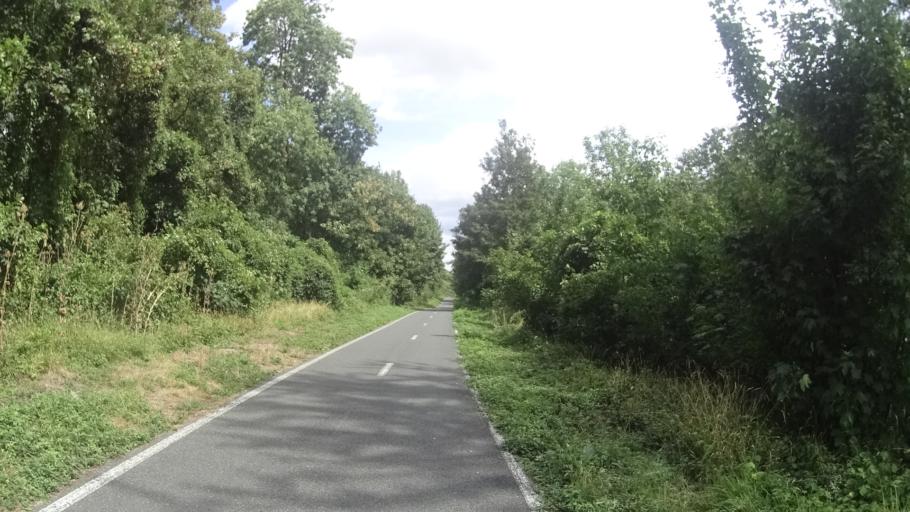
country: FR
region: Ile-de-France
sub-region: Departement de Seine-et-Marne
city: Villeparisis
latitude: 48.9529
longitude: 2.6202
